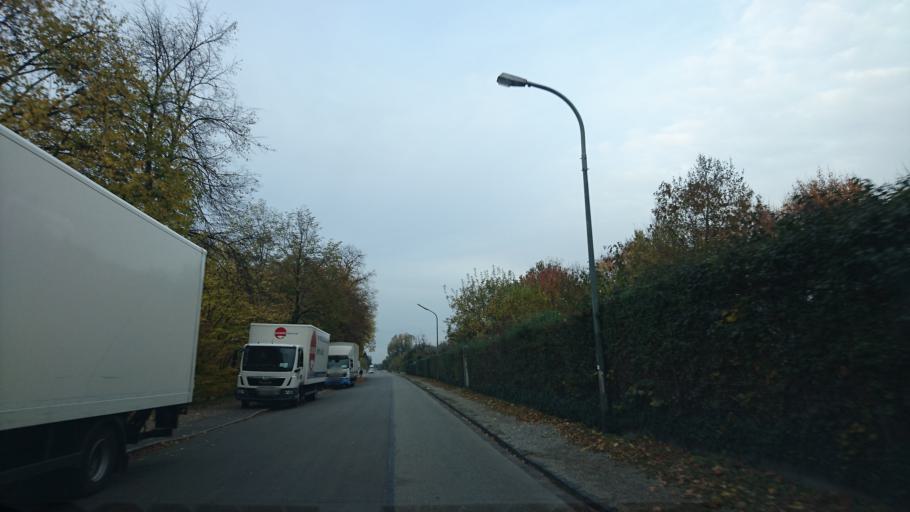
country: DE
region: Bavaria
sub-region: Swabia
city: Augsburg
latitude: 48.3865
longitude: 10.8857
